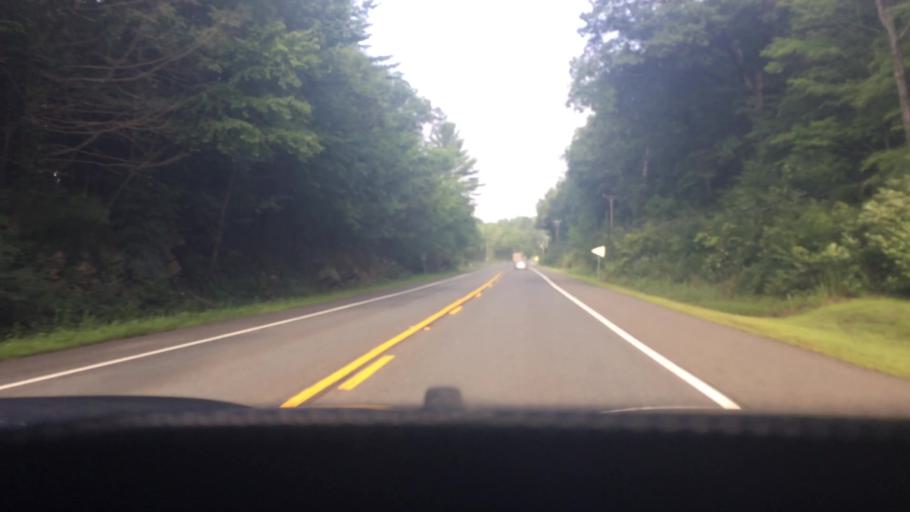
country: US
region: Massachusetts
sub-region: Franklin County
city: Millers Falls
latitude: 42.6070
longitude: -72.5189
